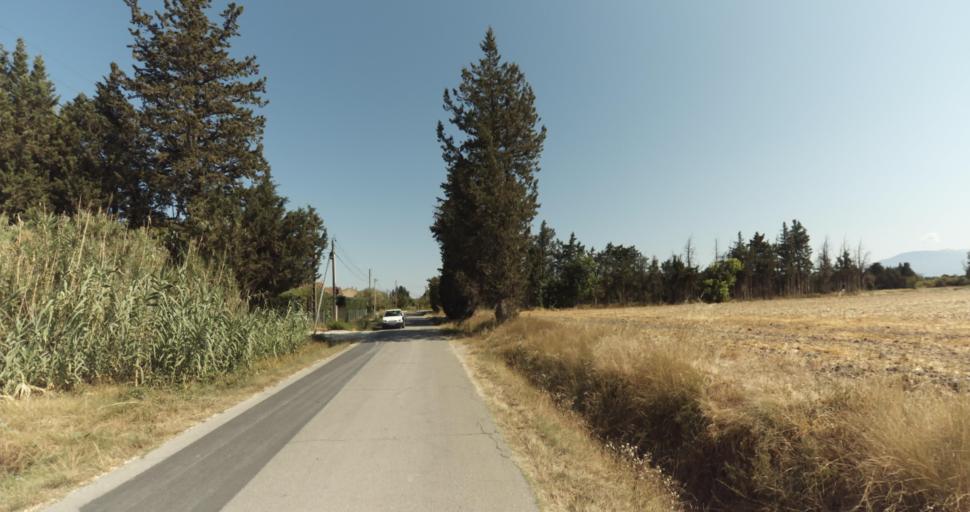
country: FR
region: Provence-Alpes-Cote d'Azur
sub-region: Departement du Vaucluse
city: Monteux
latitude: 44.0201
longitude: 4.9912
